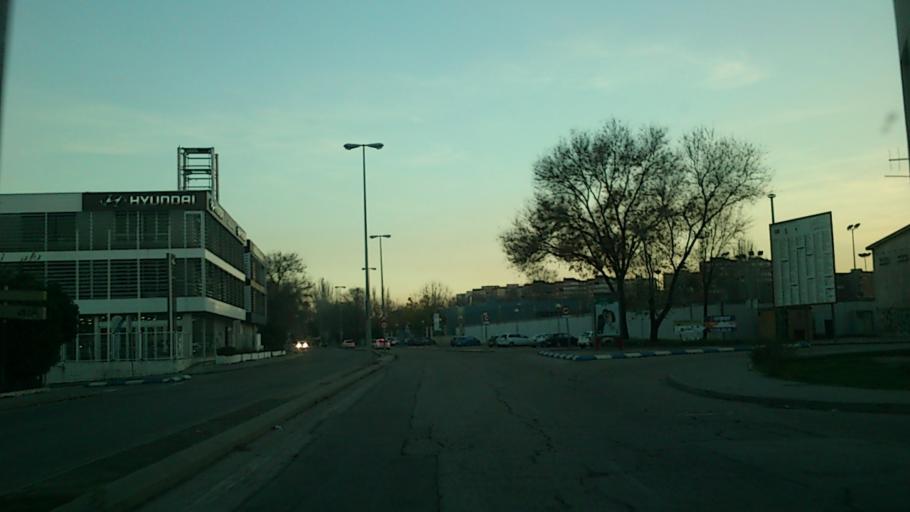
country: ES
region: Madrid
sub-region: Provincia de Madrid
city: San Fernando de Henares
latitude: 40.4358
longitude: -3.5408
